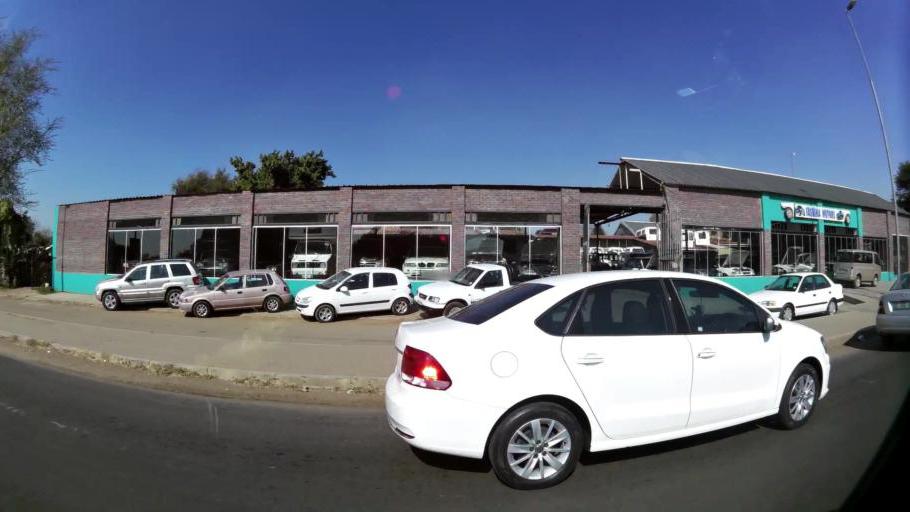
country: ZA
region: North-West
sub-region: Bojanala Platinum District Municipality
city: Rustenburg
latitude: -25.6574
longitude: 27.2424
